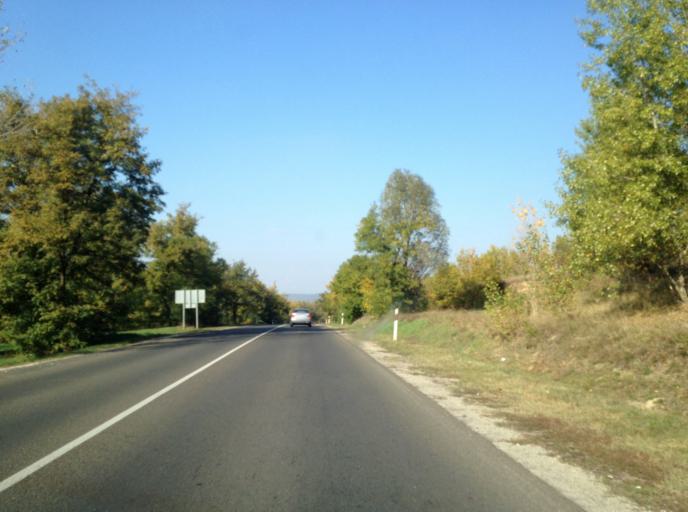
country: HU
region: Komarom-Esztergom
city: Dorog
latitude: 47.7494
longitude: 18.7379
